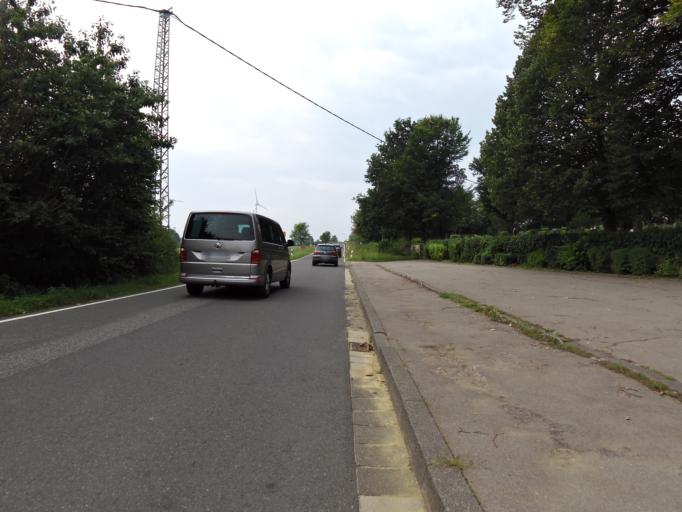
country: DE
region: Rheinland-Pfalz
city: Furfeld
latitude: 49.7758
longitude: 7.8861
